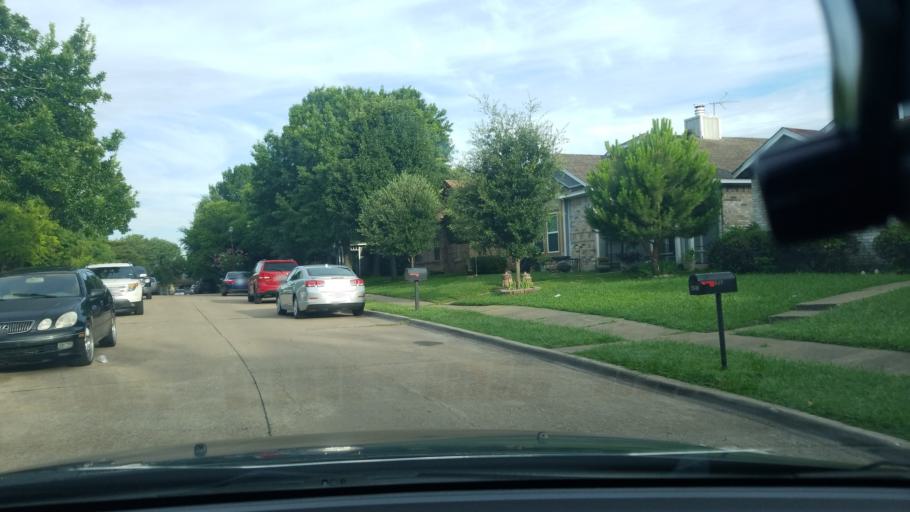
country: US
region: Texas
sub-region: Dallas County
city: Balch Springs
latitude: 32.7578
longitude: -96.6459
